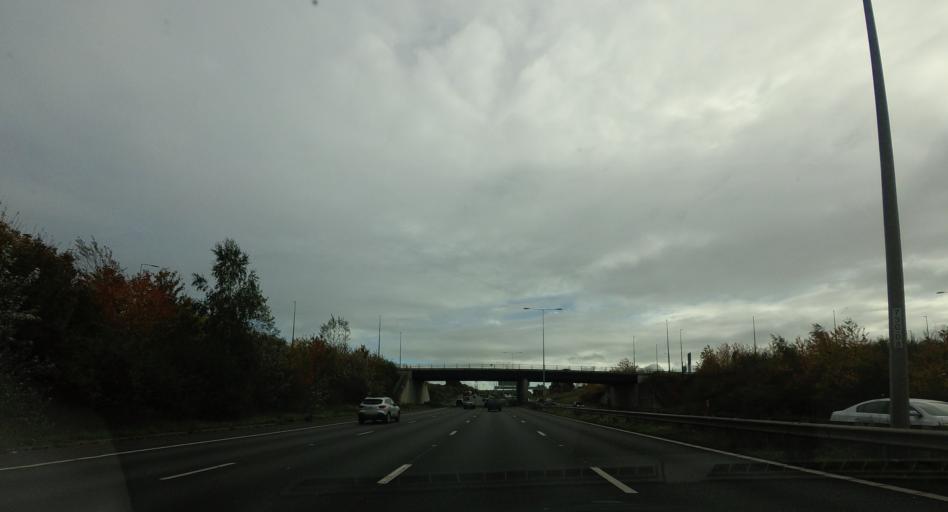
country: GB
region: England
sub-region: Kent
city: Gravesend
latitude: 51.4087
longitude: 0.3834
